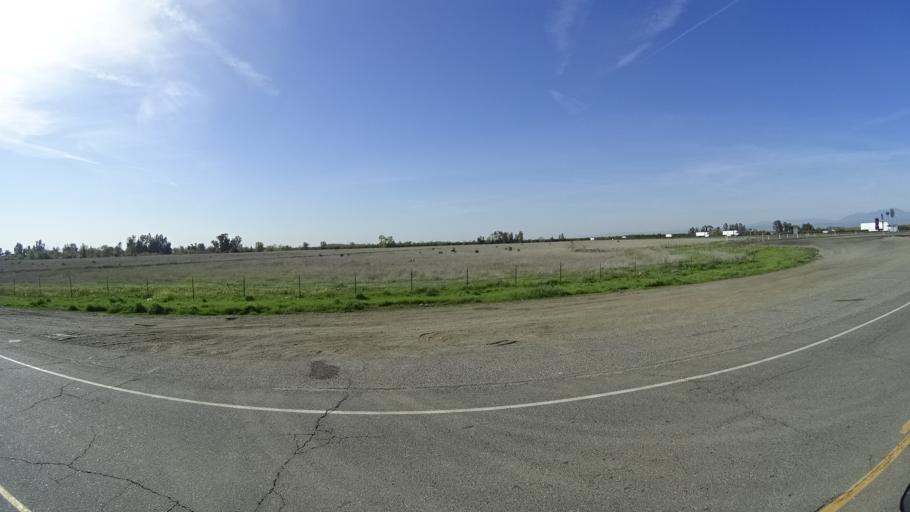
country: US
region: California
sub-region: Glenn County
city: Willows
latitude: 39.6245
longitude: -122.2029
